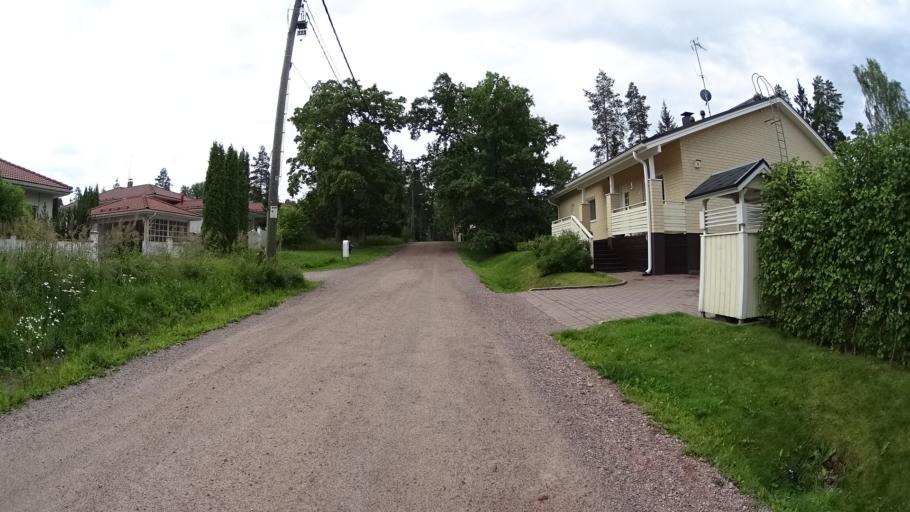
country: FI
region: Uusimaa
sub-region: Helsinki
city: Kilo
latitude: 60.2325
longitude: 24.8063
